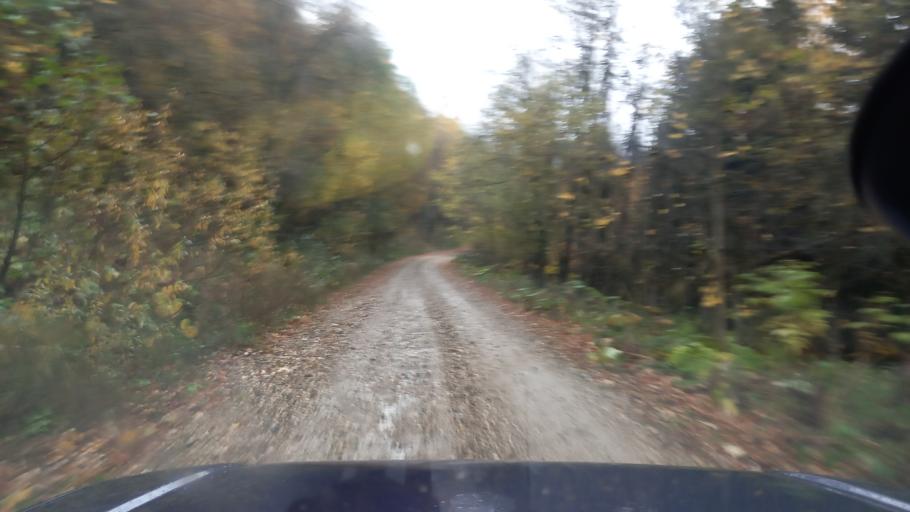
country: RU
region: Krasnodarskiy
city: Neftegorsk
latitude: 44.0365
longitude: 39.8356
